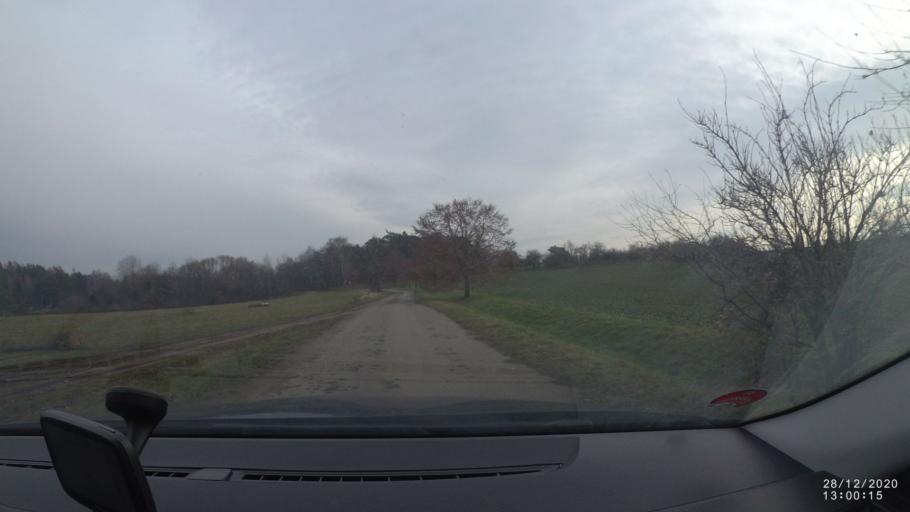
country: CZ
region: Praha
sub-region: Praha 19
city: Satalice
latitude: 50.1467
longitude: 14.6003
